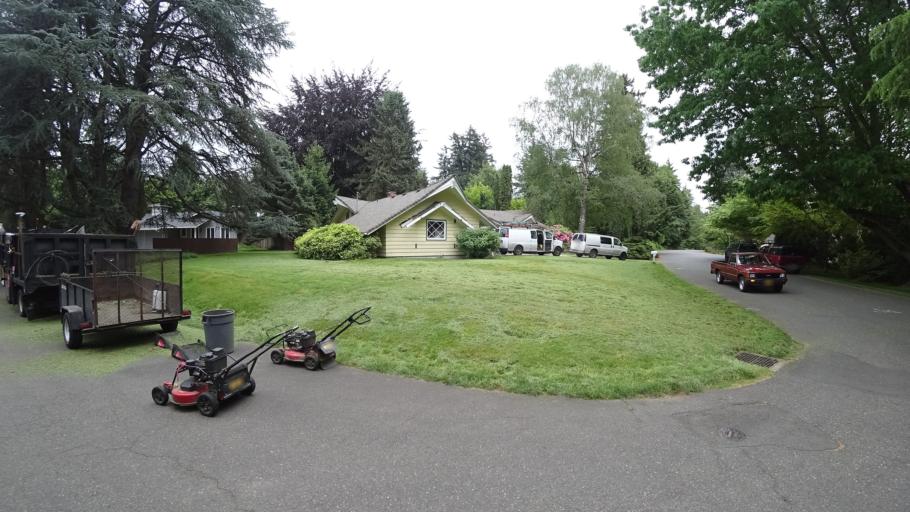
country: US
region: Oregon
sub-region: Washington County
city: Garden Home-Whitford
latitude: 45.4746
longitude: -122.7419
